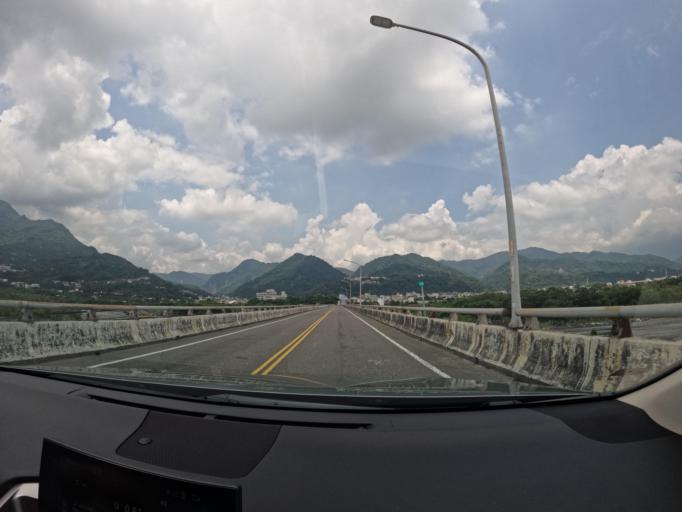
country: TW
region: Taiwan
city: Lugu
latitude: 23.8093
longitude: 120.8454
